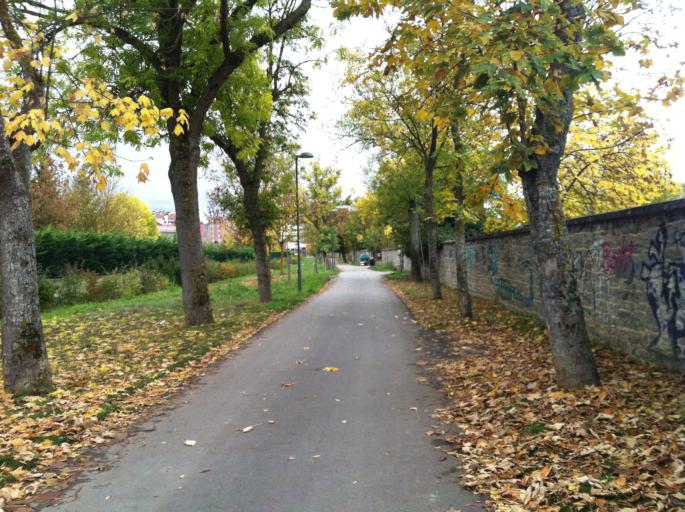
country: ES
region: Basque Country
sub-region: Provincia de Alava
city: Gasteiz / Vitoria
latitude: 42.8499
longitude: -2.6896
